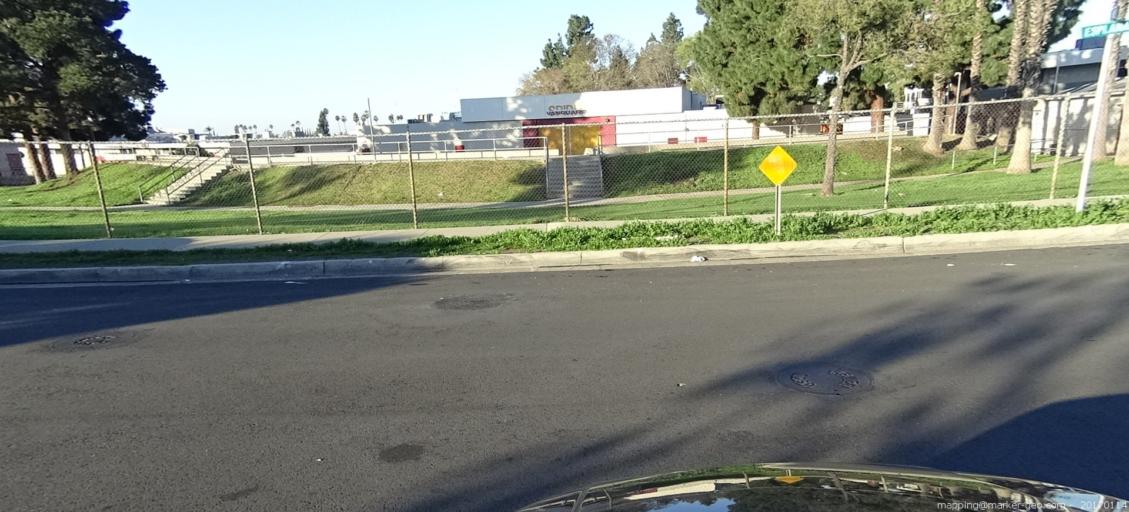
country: US
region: California
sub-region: Orange County
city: Villa Park
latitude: 33.7905
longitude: -117.8094
